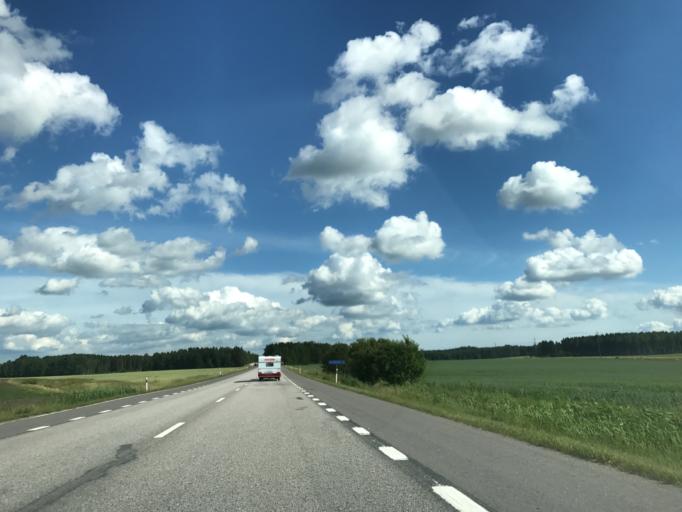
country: SE
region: Soedermanland
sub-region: Nykopings Kommun
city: Stigtomta
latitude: 58.7943
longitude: 16.7937
